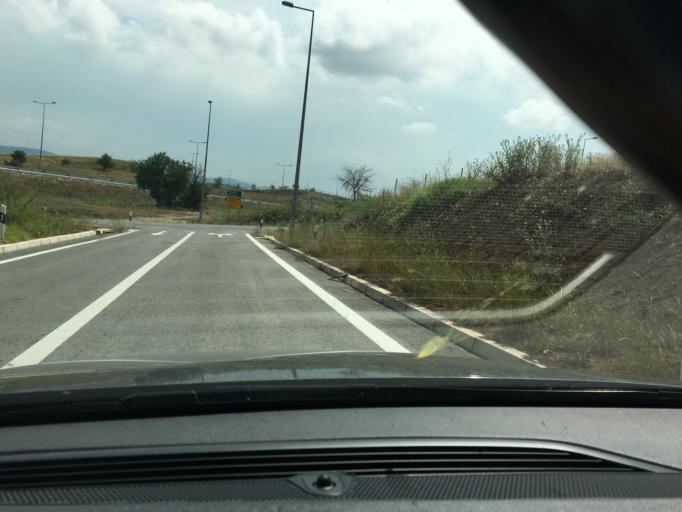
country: MK
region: Sveti Nikole
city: Gorobinci
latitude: 41.9160
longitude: 21.8780
